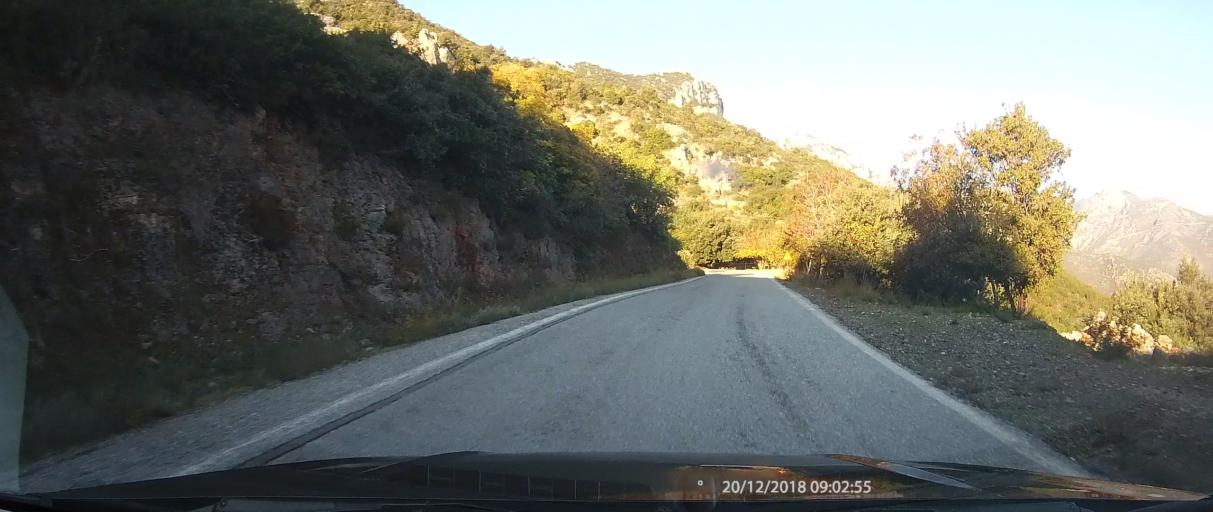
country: GR
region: Peloponnese
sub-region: Nomos Lakonias
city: Sykea
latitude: 36.9539
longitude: 22.9919
